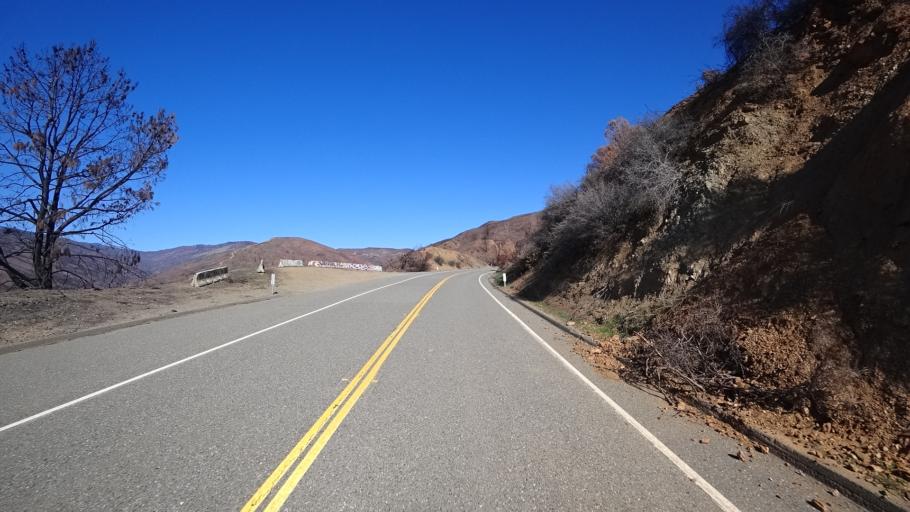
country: US
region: California
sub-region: Glenn County
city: Orland
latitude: 39.6444
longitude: -122.6082
